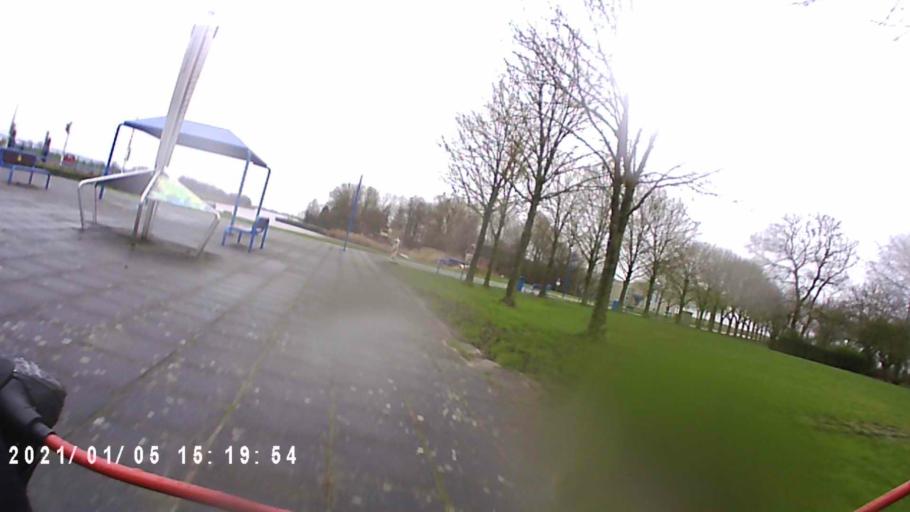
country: DE
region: Lower Saxony
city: Bunde
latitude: 53.2314
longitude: 7.2078
